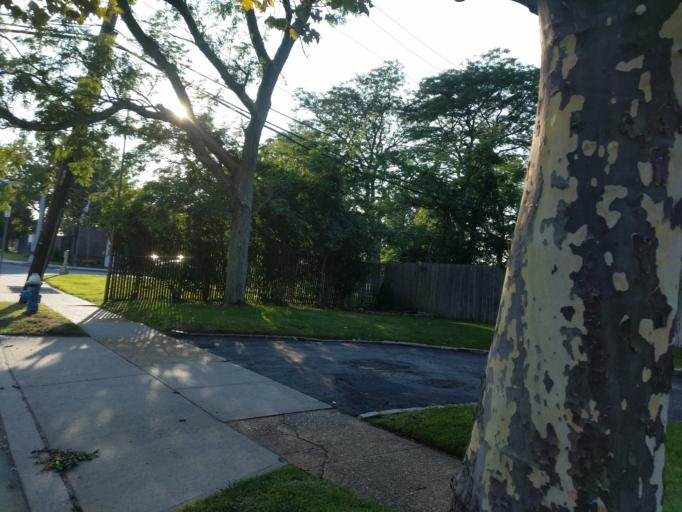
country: US
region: New York
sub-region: Nassau County
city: South Valley Stream
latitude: 40.6436
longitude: -73.7341
